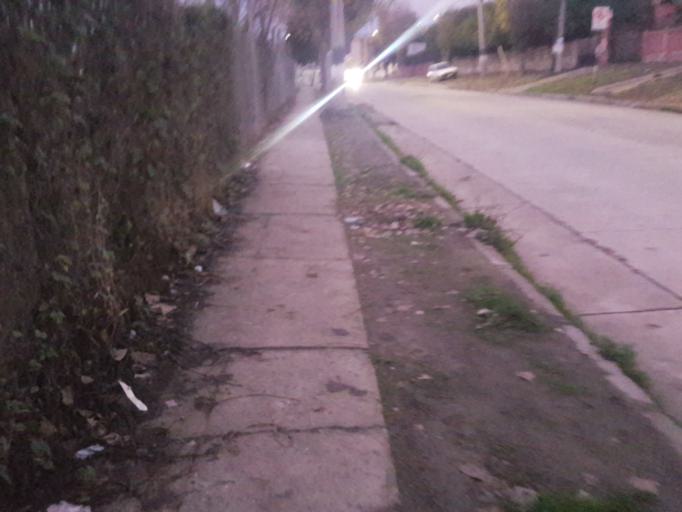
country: CL
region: Valparaiso
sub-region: Provincia de Marga Marga
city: Villa Alemana
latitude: -33.0400
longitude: -71.3516
